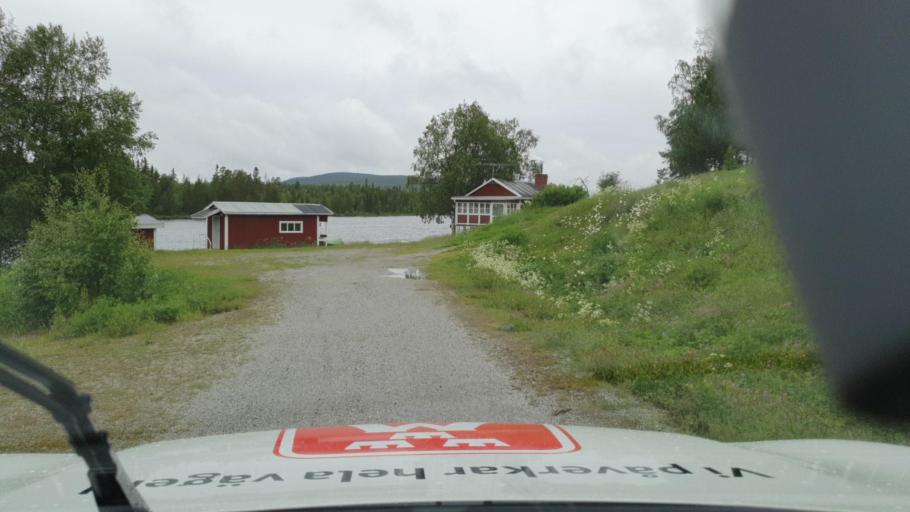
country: SE
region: Vaesterbotten
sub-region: Asele Kommun
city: Asele
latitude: 63.9438
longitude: 17.2660
